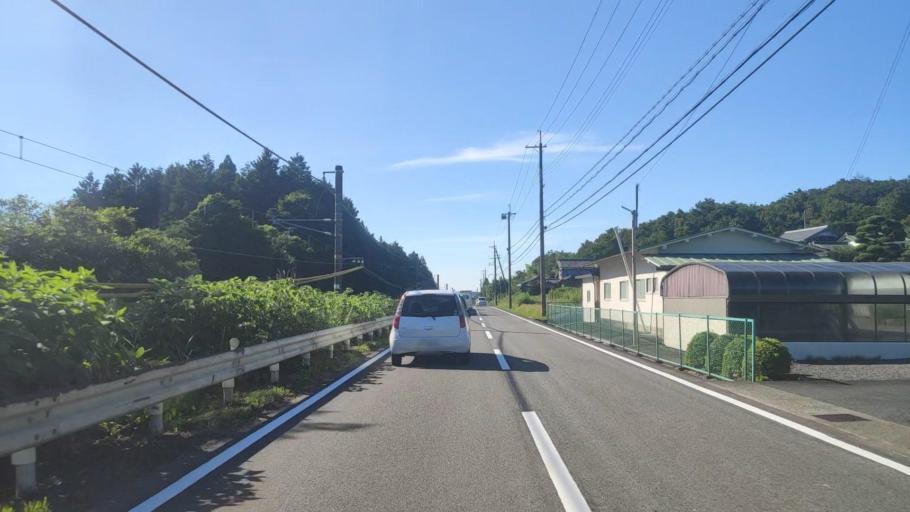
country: JP
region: Shiga Prefecture
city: Minakuchicho-matoba
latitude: 34.8785
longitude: 136.2377
